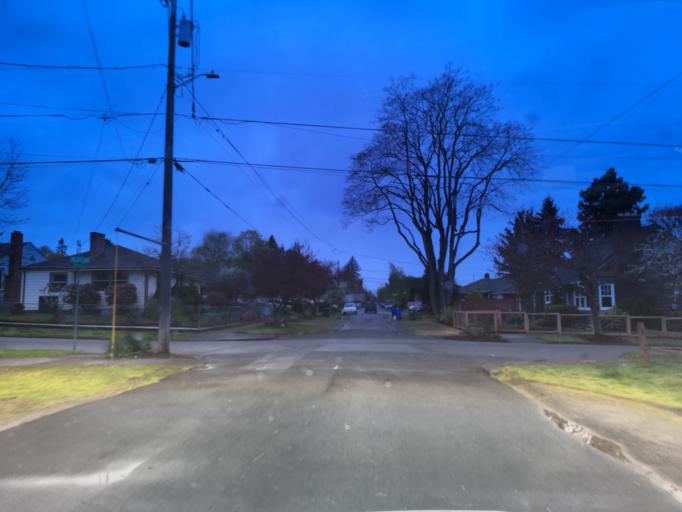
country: US
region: Oregon
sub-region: Multnomah County
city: Lents
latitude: 45.5539
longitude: -122.5959
